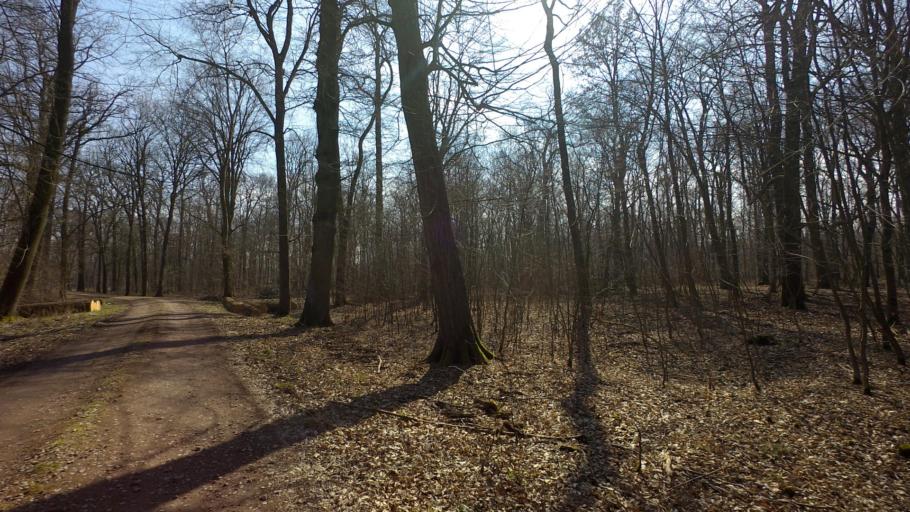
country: DE
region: Saxony-Anhalt
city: Vockerode
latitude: 51.8609
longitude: 12.3234
